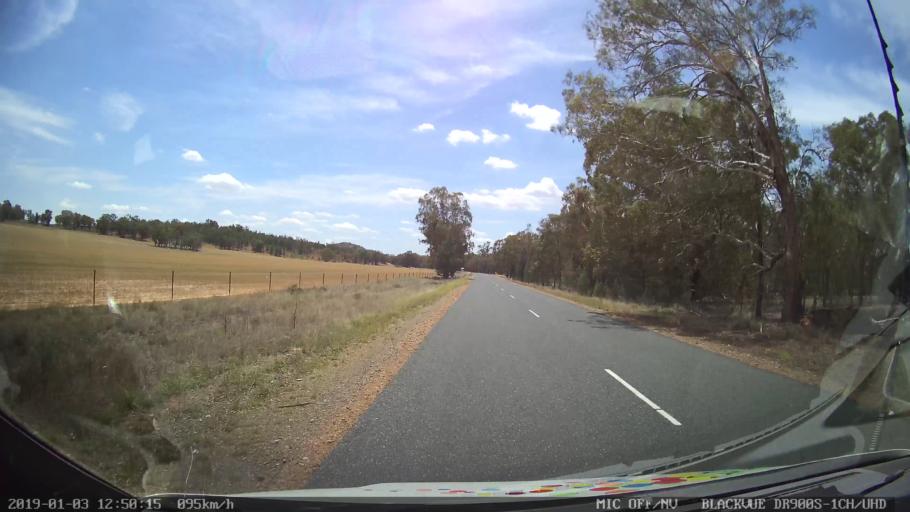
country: AU
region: New South Wales
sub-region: Weddin
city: Grenfell
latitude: -33.6935
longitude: 148.2682
